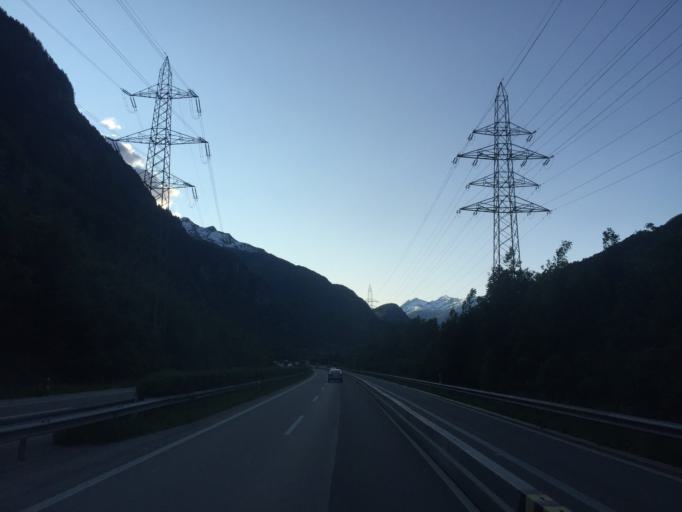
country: CH
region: Ticino
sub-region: Leventina District
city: Bodio
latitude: 46.3873
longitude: 8.8890
